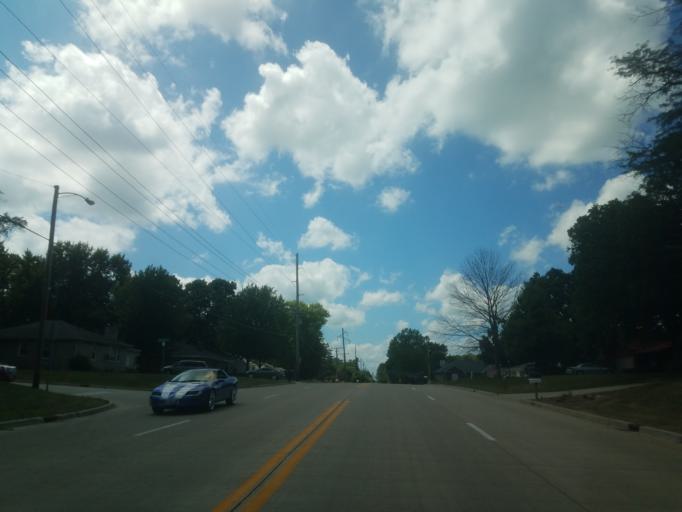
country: US
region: Illinois
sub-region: McLean County
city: Bloomington
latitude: 40.4590
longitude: -89.0092
